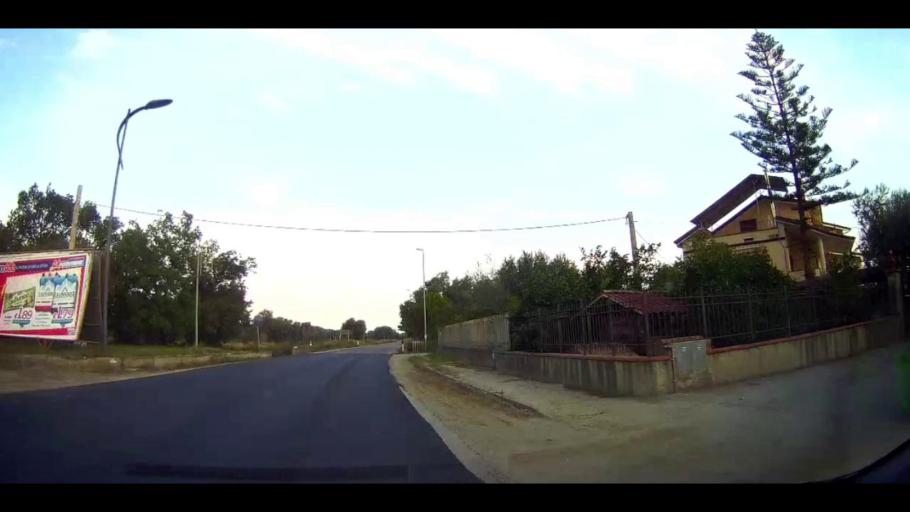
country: IT
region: Calabria
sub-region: Provincia di Crotone
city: Torretta
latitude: 39.4607
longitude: 17.0290
